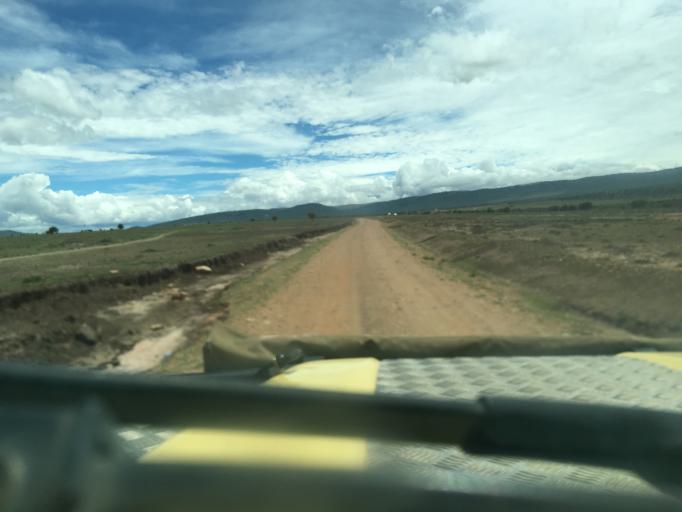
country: TZ
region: Mara
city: Mugumu
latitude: -1.9551
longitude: 35.4885
